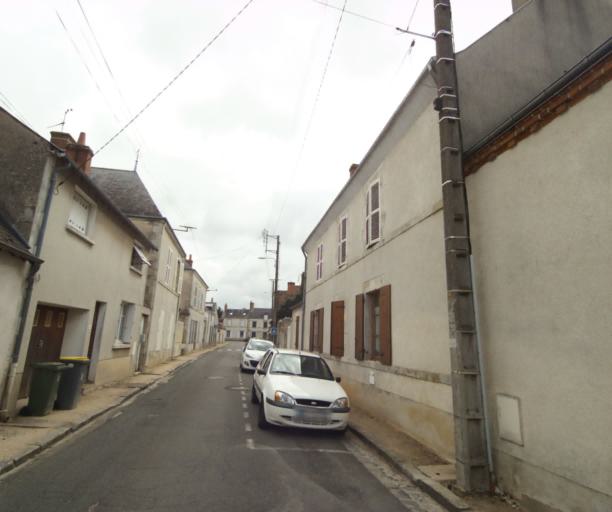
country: FR
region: Centre
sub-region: Departement du Loiret
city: Mardie
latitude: 47.8737
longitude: 2.0472
